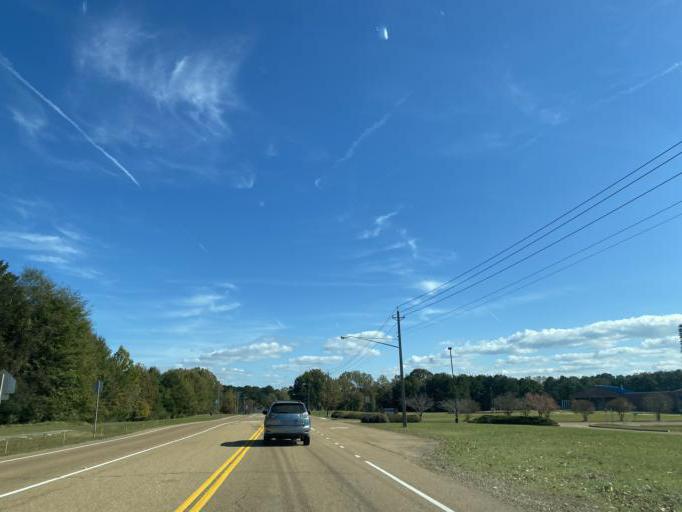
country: US
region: Mississippi
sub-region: Madison County
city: Madison
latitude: 32.4575
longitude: -90.0928
